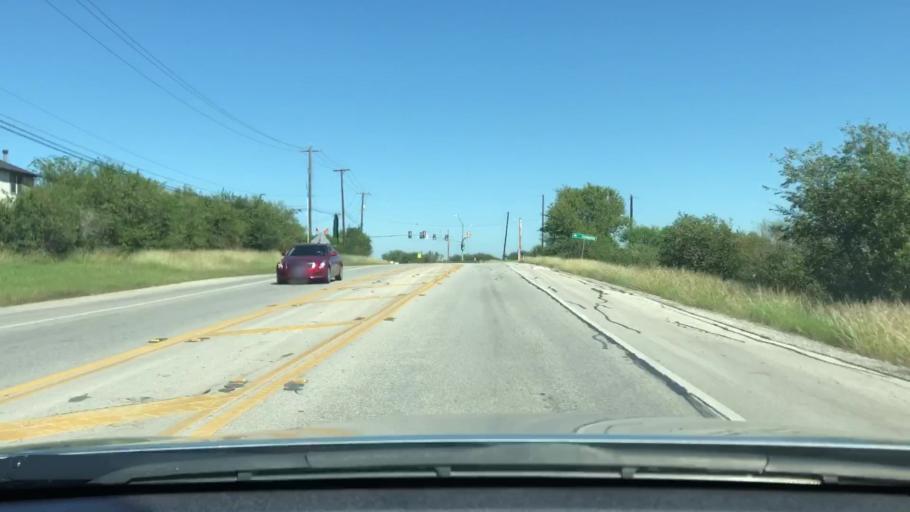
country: US
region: Texas
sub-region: Bexar County
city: Converse
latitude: 29.4884
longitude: -98.3106
